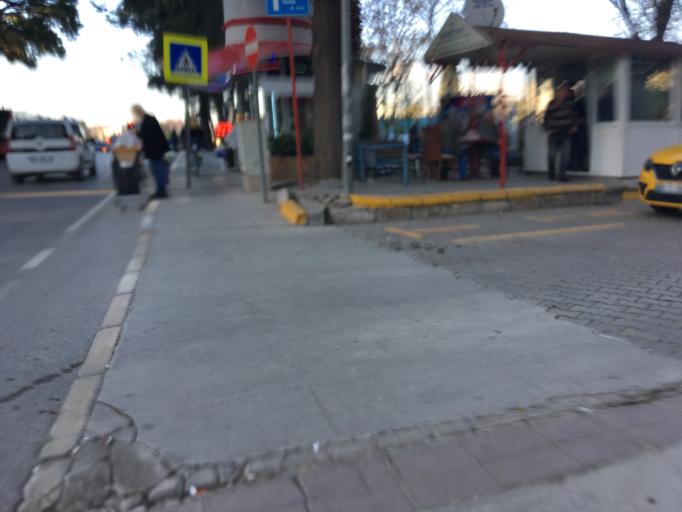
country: TR
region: Izmir
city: Buca
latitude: 38.3854
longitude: 27.1662
